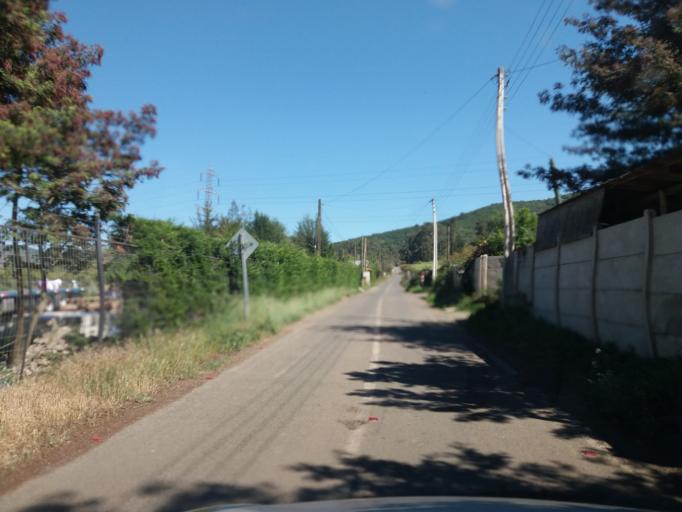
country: CL
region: Valparaiso
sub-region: Provincia de Quillota
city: Quillota
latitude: -32.8588
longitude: -71.2687
